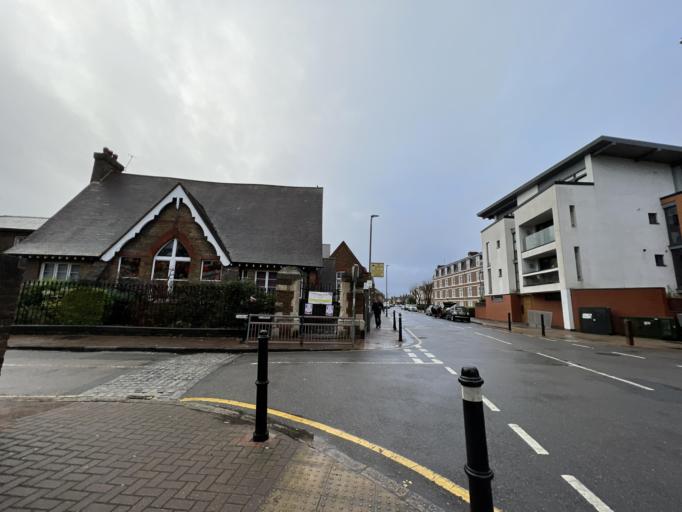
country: GB
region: England
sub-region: Greater London
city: Wandsworth
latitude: 51.4661
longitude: -0.2202
